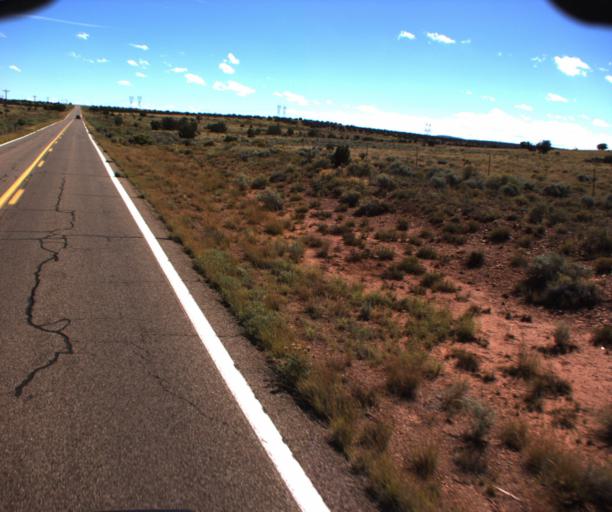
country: US
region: Arizona
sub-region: Apache County
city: Saint Johns
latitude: 34.5690
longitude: -109.6338
